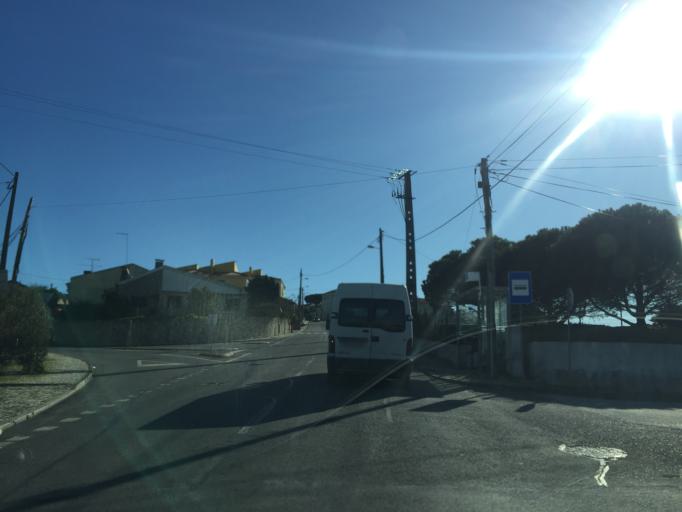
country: PT
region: Lisbon
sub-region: Sintra
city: Almargem
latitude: 38.8262
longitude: -9.2997
